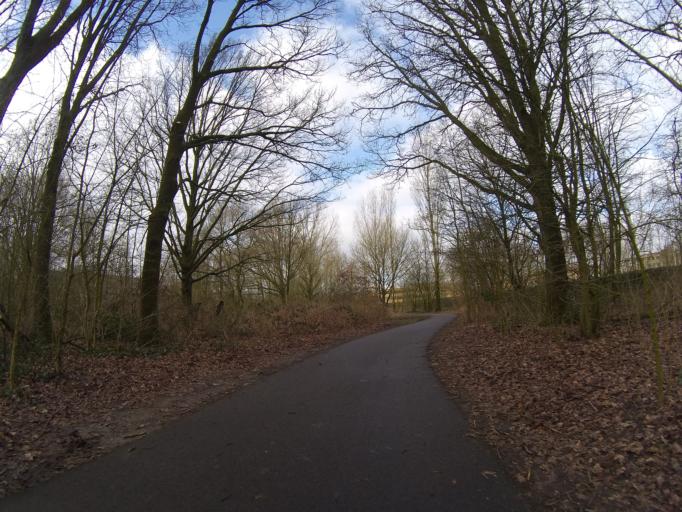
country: NL
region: Utrecht
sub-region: Gemeente Amersfoort
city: Randenbroek
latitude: 52.1722
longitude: 5.4069
